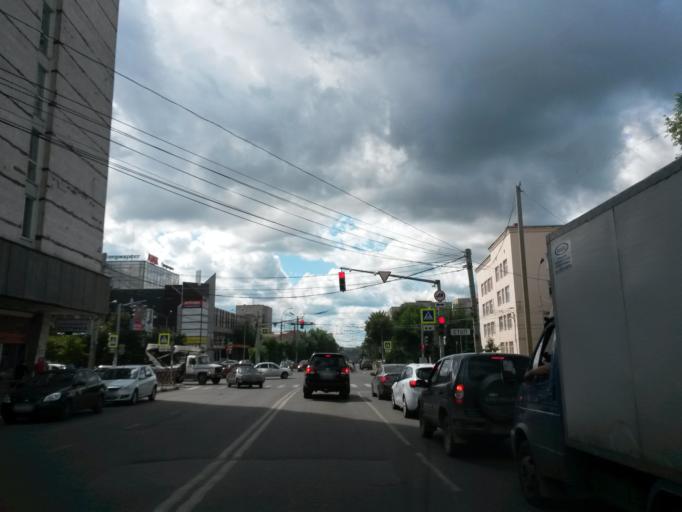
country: RU
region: Jaroslavl
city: Yaroslavl
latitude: 57.6274
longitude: 39.8487
